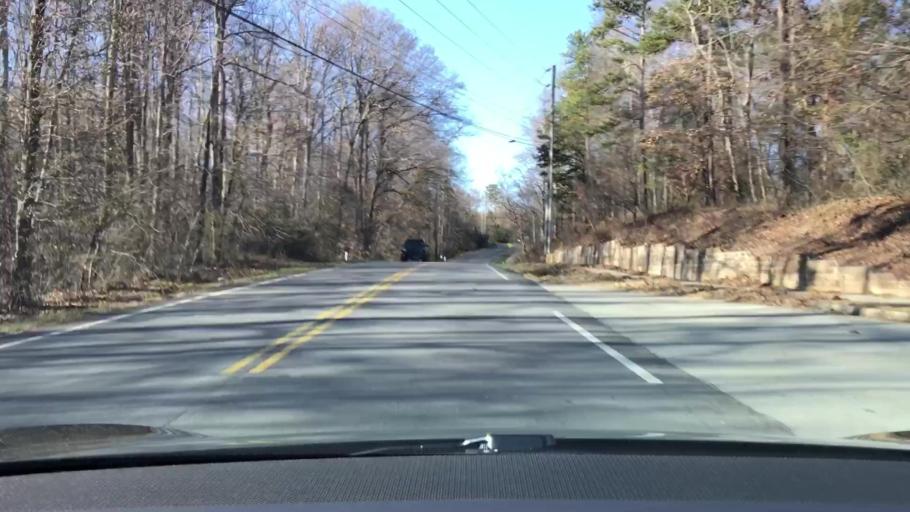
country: US
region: Georgia
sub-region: Barrow County
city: Auburn
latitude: 34.0660
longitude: -83.8530
